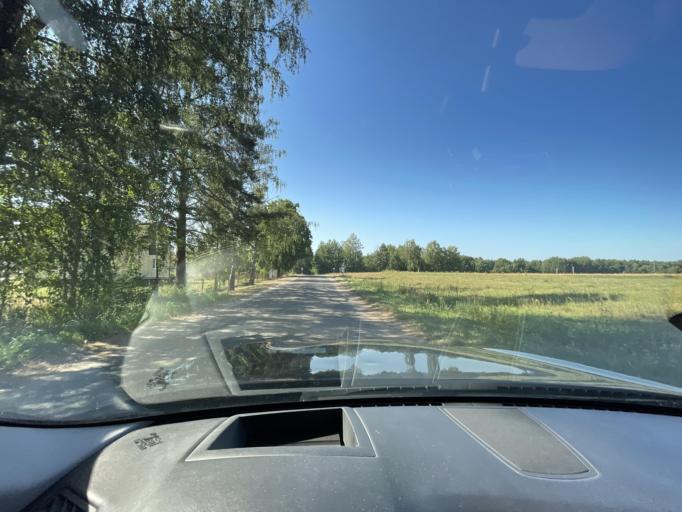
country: BY
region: Grodnenskaya
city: Hrodna
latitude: 53.7595
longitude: 23.9652
